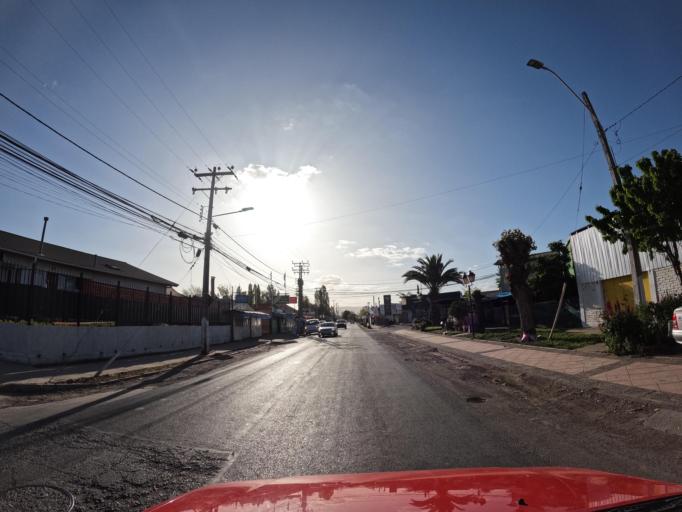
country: CL
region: O'Higgins
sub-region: Provincia de Colchagua
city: Santa Cruz
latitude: -34.6484
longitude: -71.3575
